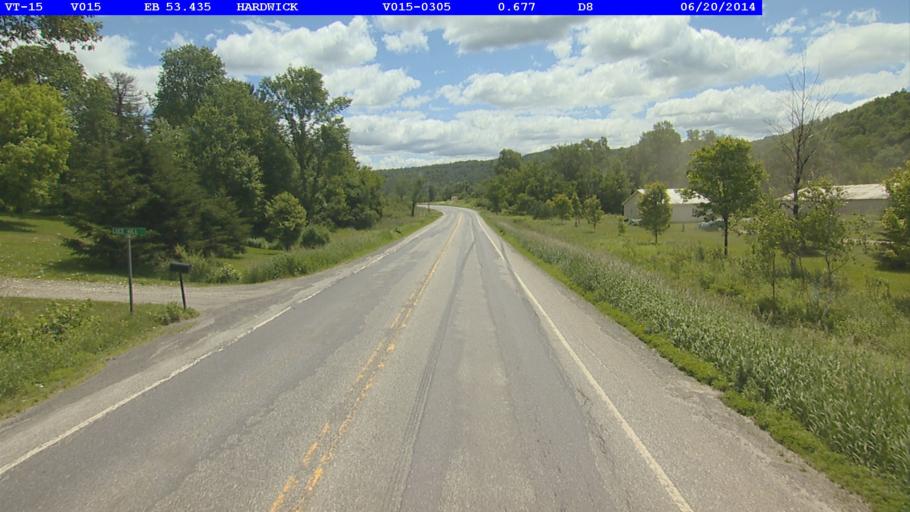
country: US
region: Vermont
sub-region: Caledonia County
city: Hardwick
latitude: 44.5191
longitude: -72.4084
